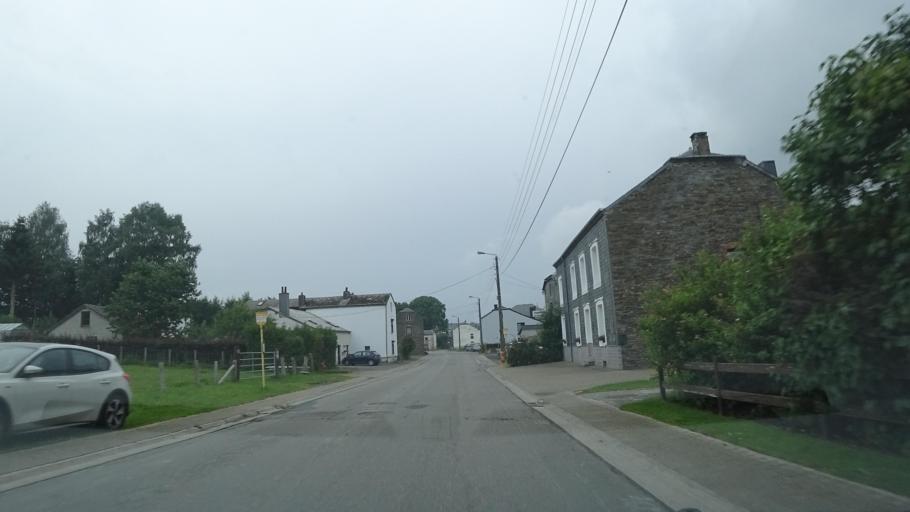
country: BE
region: Wallonia
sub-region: Province du Luxembourg
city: Bertrix
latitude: 49.8328
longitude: 5.3002
